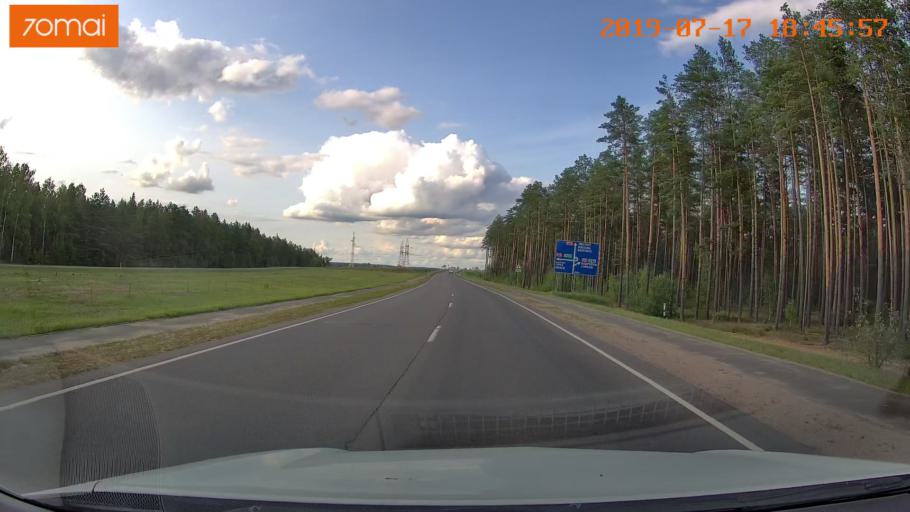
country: BY
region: Mogilev
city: Asipovichy
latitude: 53.3302
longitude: 28.6610
